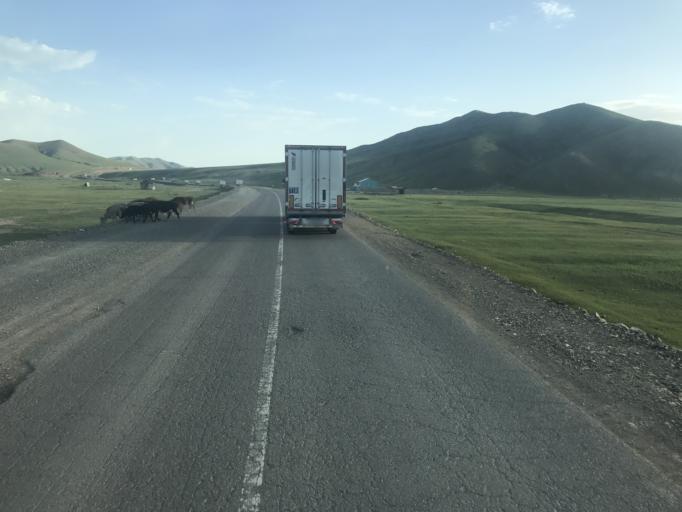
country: MN
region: Central Aimak
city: Bornuur
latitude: 48.3889
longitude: 106.2118
